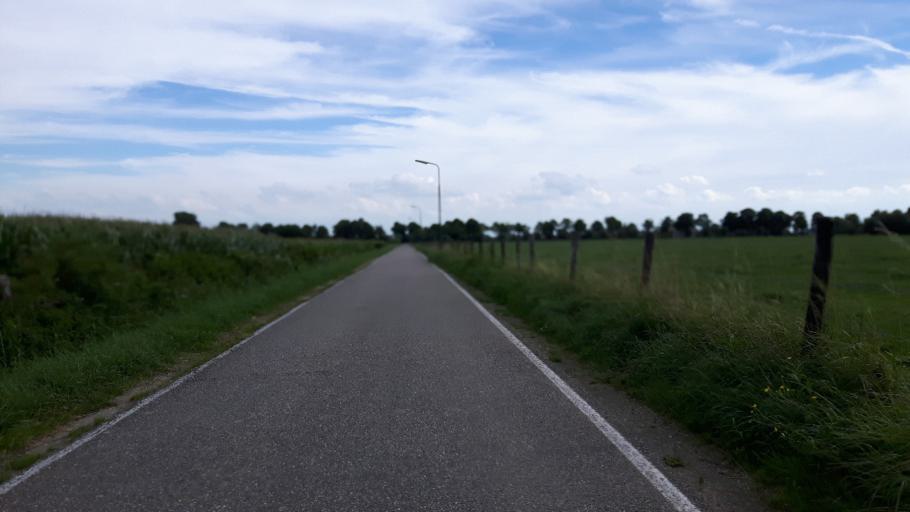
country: NL
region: Utrecht
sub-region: Gemeente Montfoort
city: Montfoort
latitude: 52.0927
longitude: 4.9755
